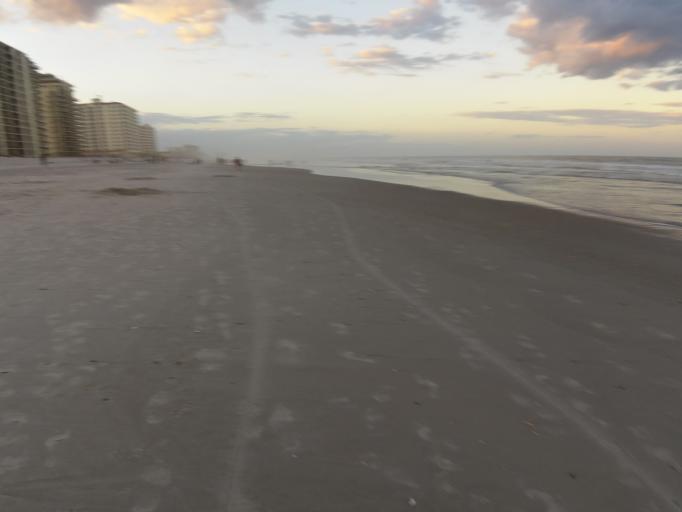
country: US
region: Florida
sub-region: Duval County
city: Jacksonville Beach
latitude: 30.2746
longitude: -81.3852
